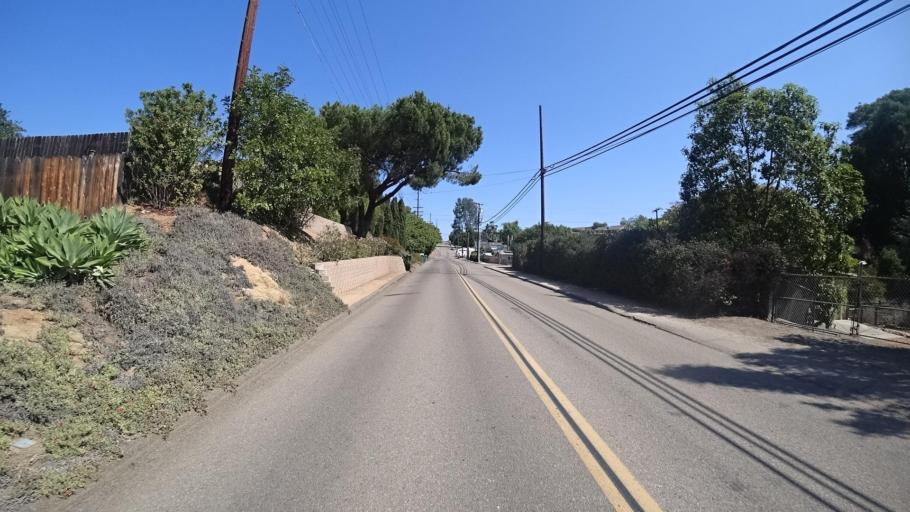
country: US
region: California
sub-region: San Diego County
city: Winter Gardens
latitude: 32.8281
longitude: -116.9232
